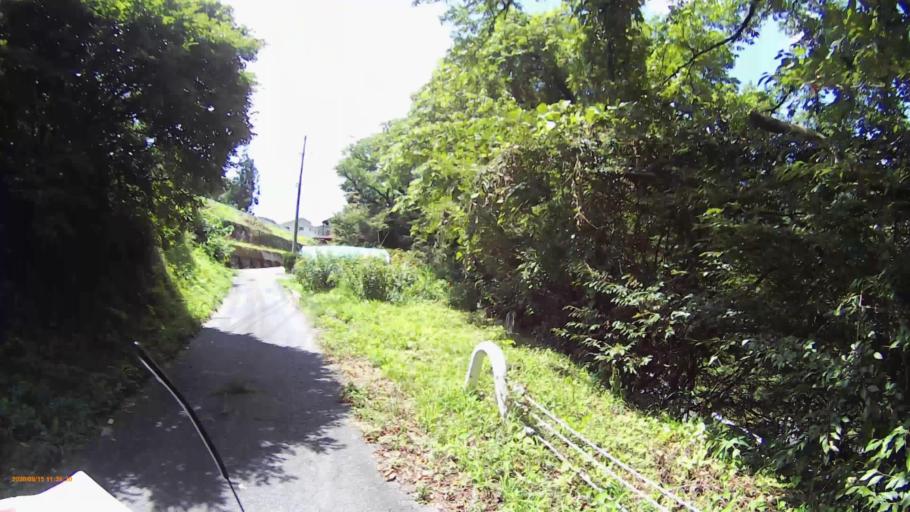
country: JP
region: Nagano
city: Ina
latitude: 35.8343
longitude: 137.6856
